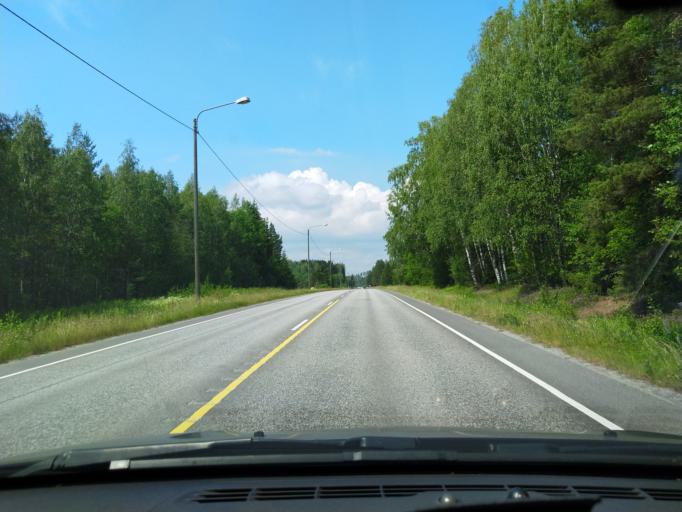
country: FI
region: Uusimaa
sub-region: Helsinki
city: Saukkola
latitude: 60.3775
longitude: 24.0992
